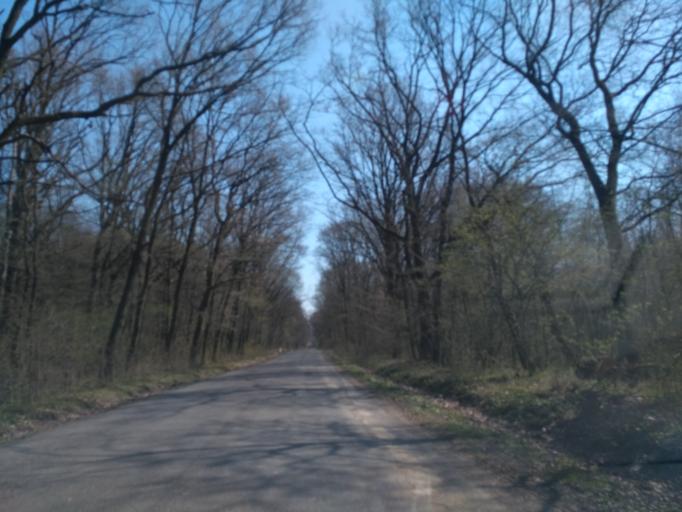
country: SK
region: Presovsky
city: Vranov nad Topl'ou
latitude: 48.7990
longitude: 21.6573
